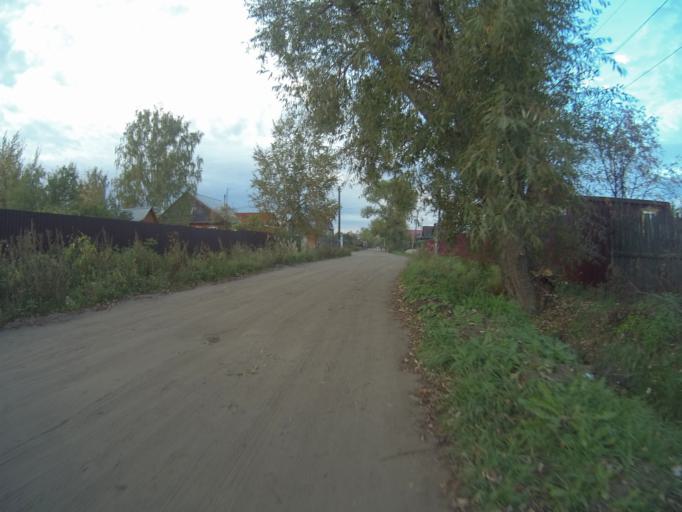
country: RU
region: Vladimir
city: Sobinka
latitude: 55.9831
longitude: 40.0109
